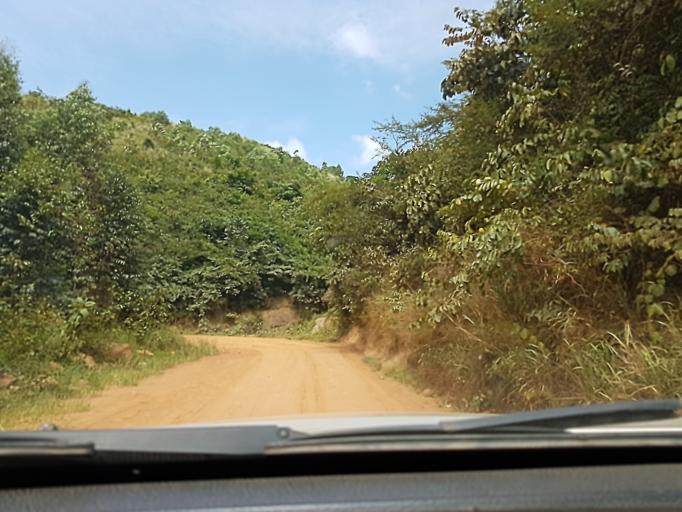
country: RW
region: Western Province
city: Cyangugu
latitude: -2.7047
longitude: 28.9494
